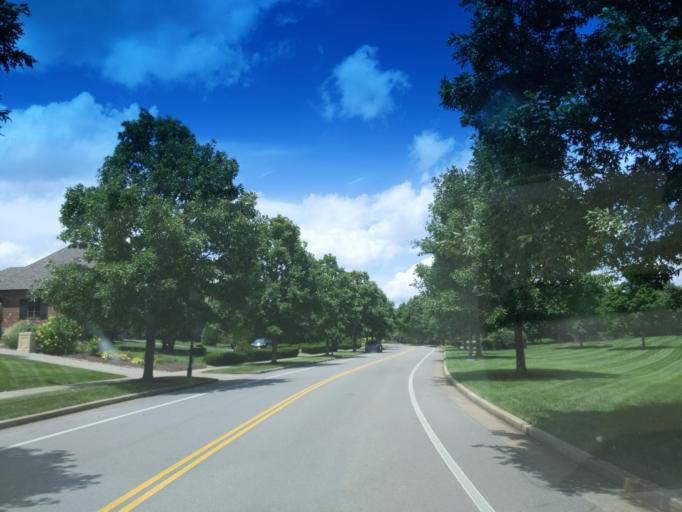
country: US
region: Tennessee
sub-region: Williamson County
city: Brentwood Estates
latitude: 36.0258
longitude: -86.7700
